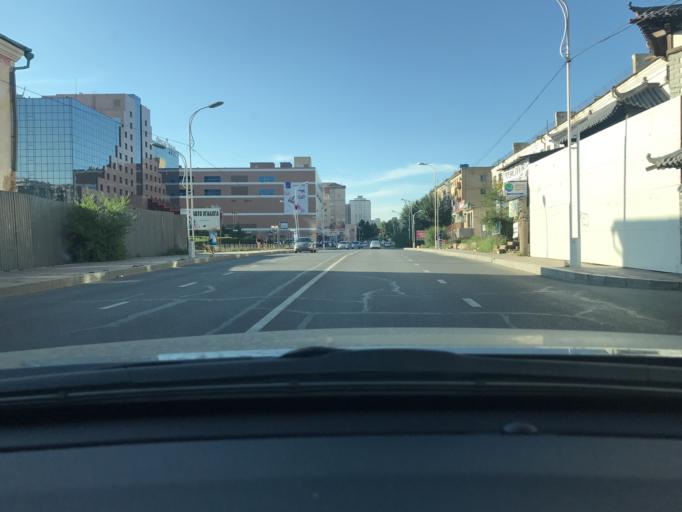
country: MN
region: Ulaanbaatar
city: Ulaanbaatar
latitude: 47.9206
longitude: 106.9351
